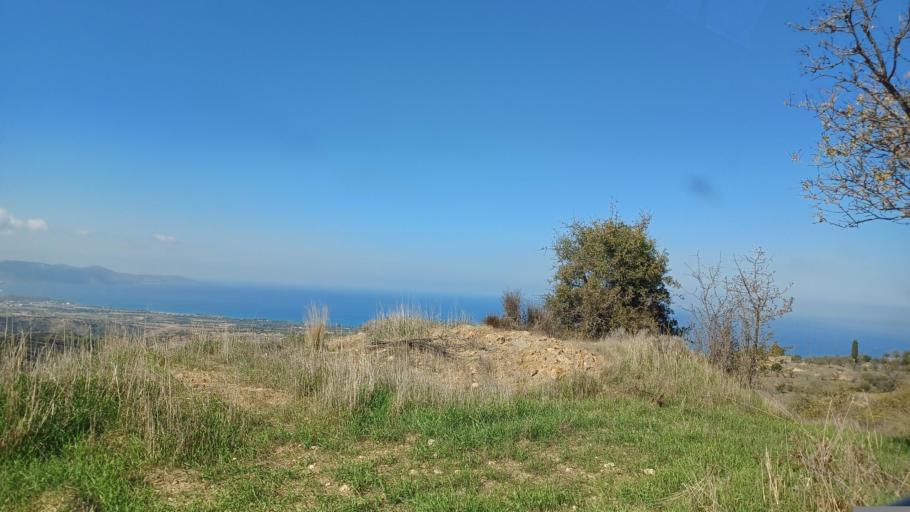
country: CY
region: Pafos
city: Polis
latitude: 35.0323
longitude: 32.5027
